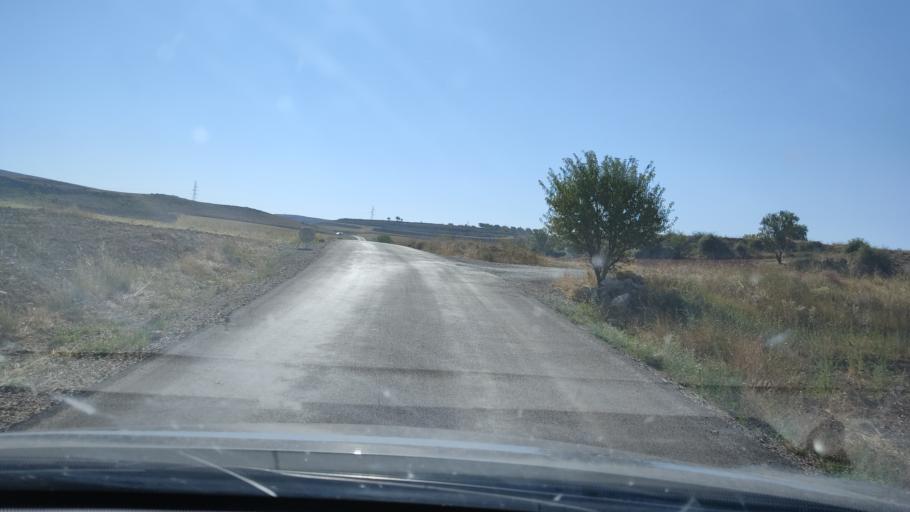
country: ES
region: Aragon
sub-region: Provincia de Teruel
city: Monforte de Moyuela
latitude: 41.0435
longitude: -0.9974
